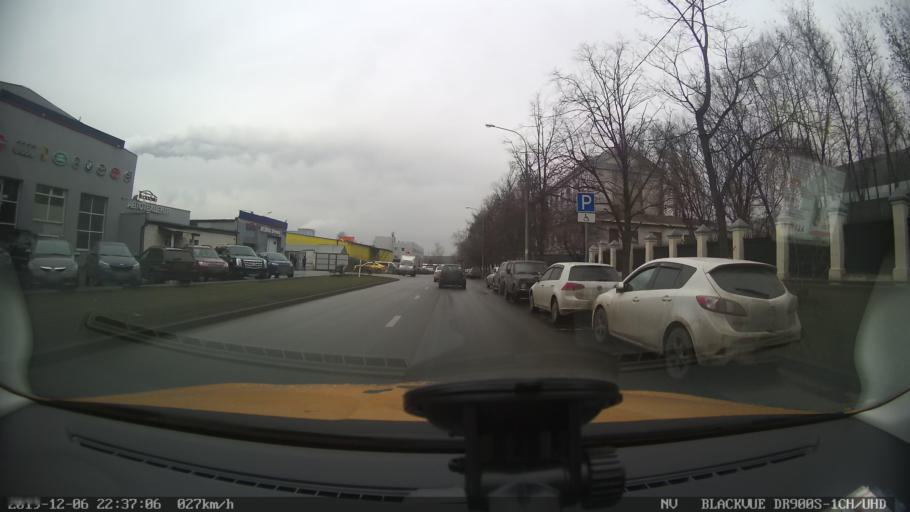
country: RU
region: Moscow
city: Metrogorodok
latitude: 55.8141
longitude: 37.7855
